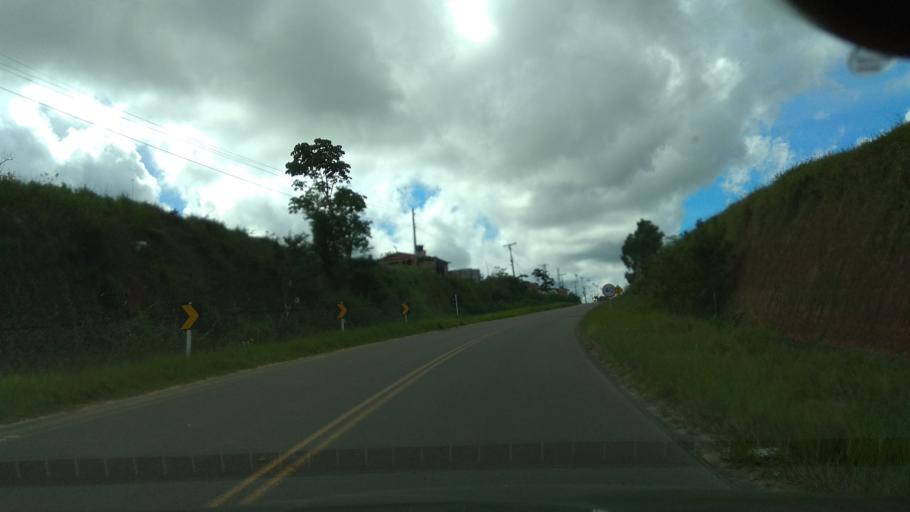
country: BR
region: Bahia
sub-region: Mutuipe
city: Mutuipe
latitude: -13.1656
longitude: -39.4096
